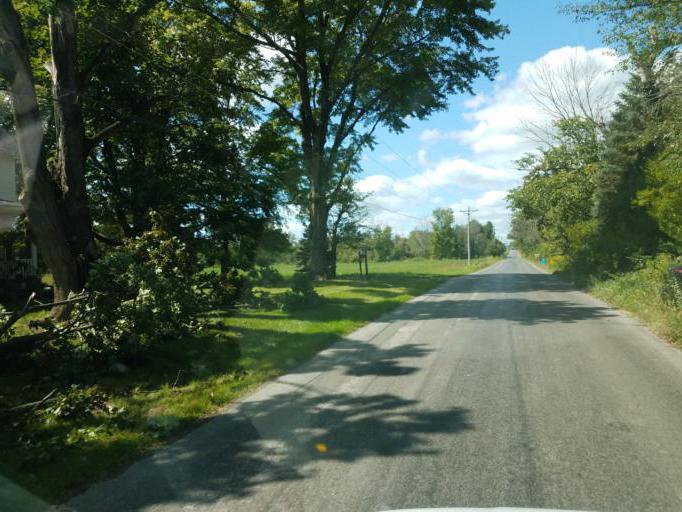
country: US
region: Ohio
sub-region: Wayne County
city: West Salem
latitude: 41.0134
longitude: -82.2136
